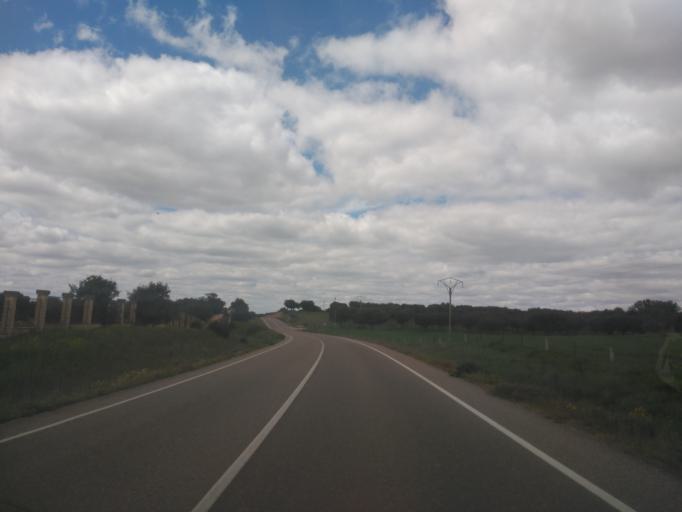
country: ES
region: Castille and Leon
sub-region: Provincia de Salamanca
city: Florida de Liebana
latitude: 41.0372
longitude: -5.7383
